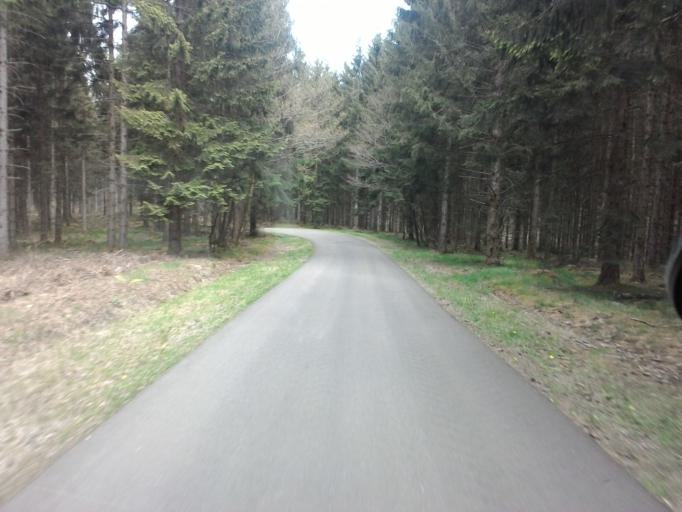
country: FR
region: Bourgogne
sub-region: Departement de la Nievre
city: Lormes
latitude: 47.3181
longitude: 3.8961
